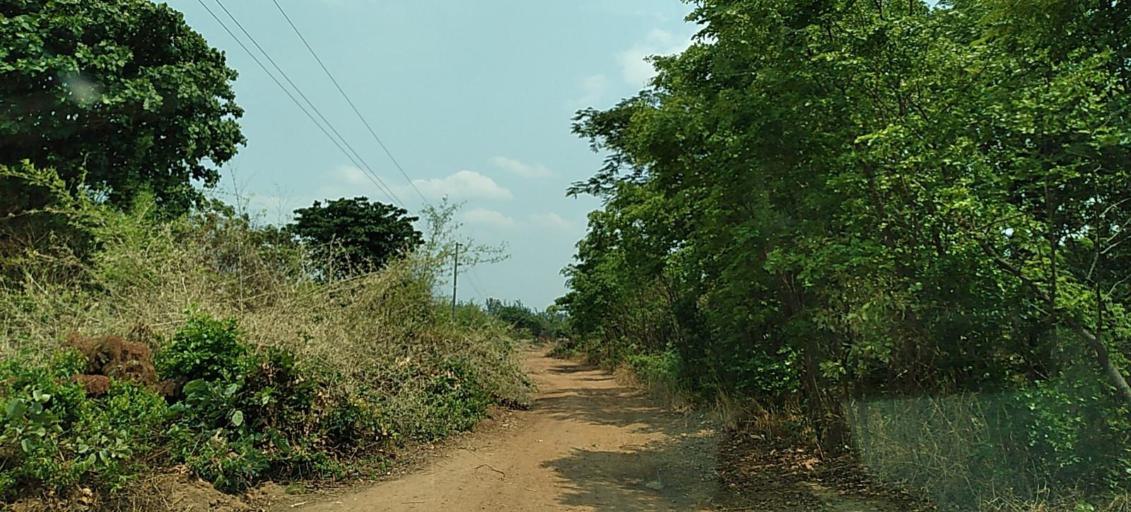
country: ZM
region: Copperbelt
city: Kalulushi
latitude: -12.7625
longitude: 28.0318
